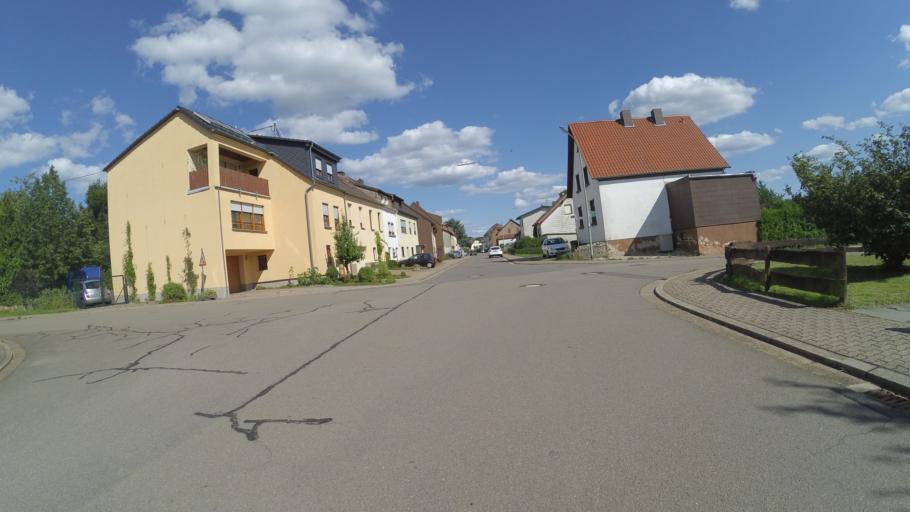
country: DE
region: Saarland
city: Illingen
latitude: 49.3891
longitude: 7.0634
